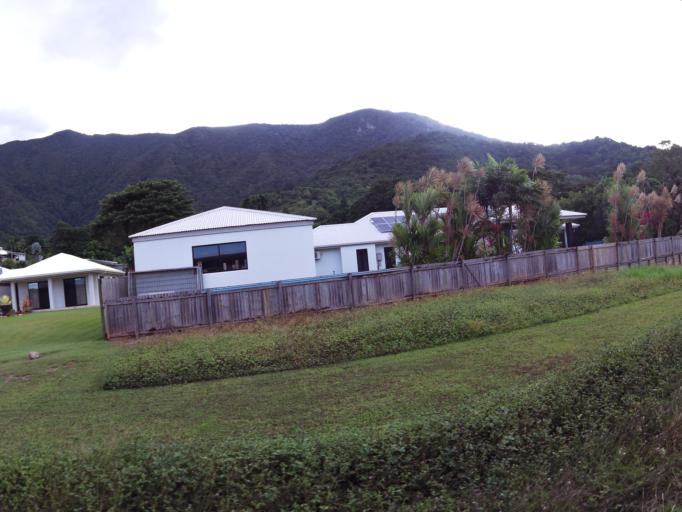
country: AU
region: Queensland
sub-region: Cairns
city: Redlynch
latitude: -16.9001
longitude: 145.6918
